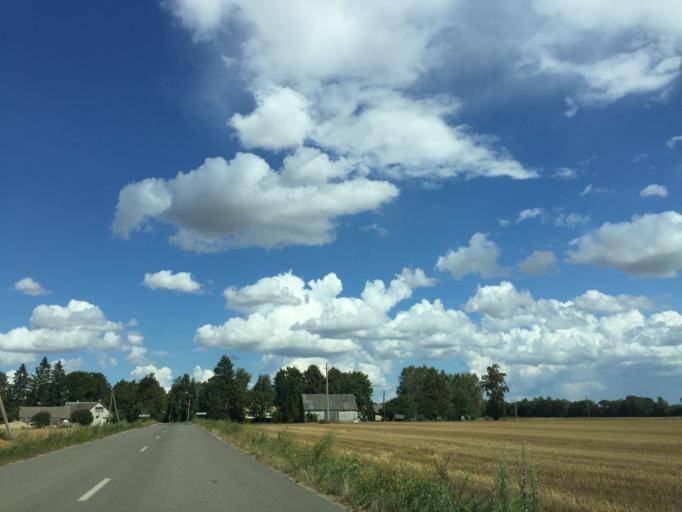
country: LV
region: Rundales
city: Pilsrundale
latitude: 56.3108
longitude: 23.9091
